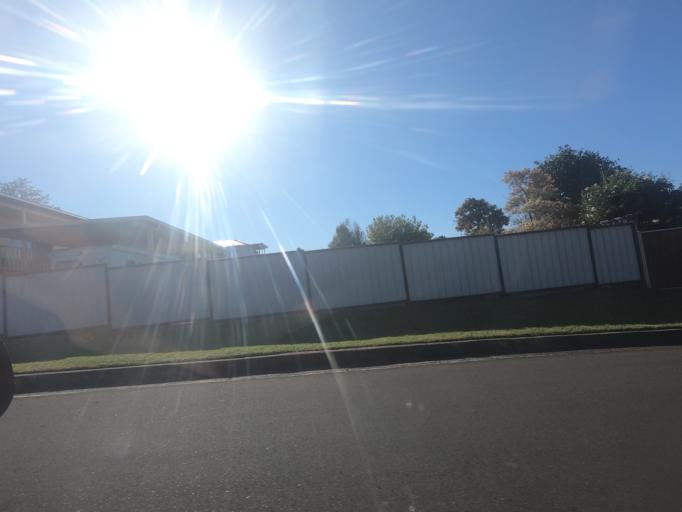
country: AU
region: New South Wales
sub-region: Wollongong
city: Corrimal
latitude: -34.3681
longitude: 150.8926
